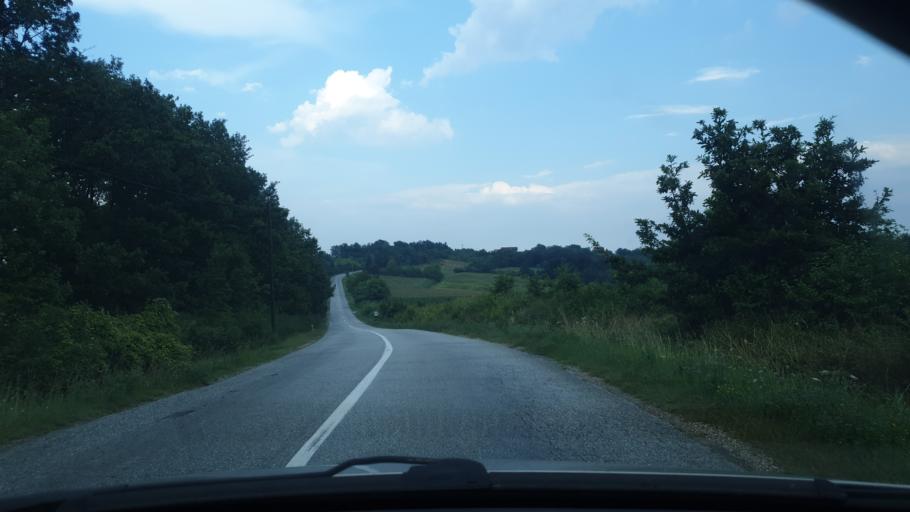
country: RS
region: Central Serbia
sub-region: Sumadijski Okrug
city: Kragujevac
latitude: 44.0456
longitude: 20.7879
